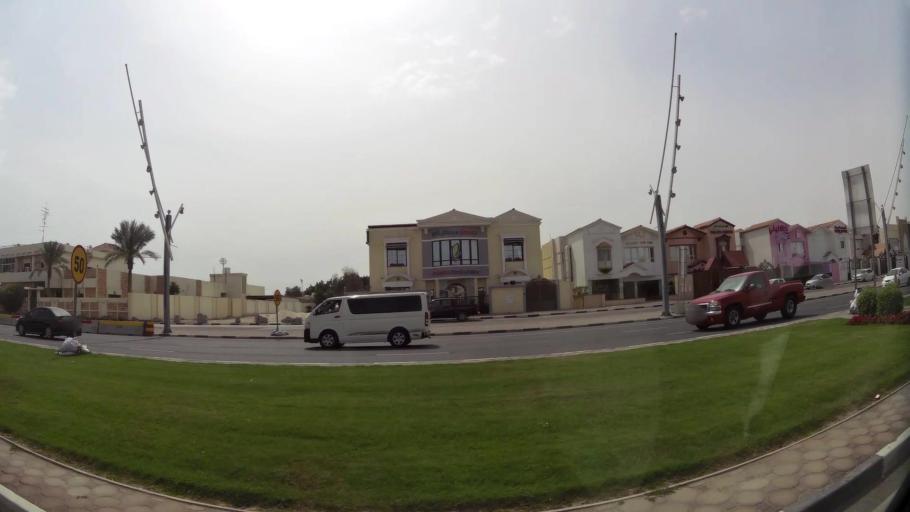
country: QA
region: Baladiyat ad Dawhah
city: Doha
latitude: 25.2723
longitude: 51.4824
